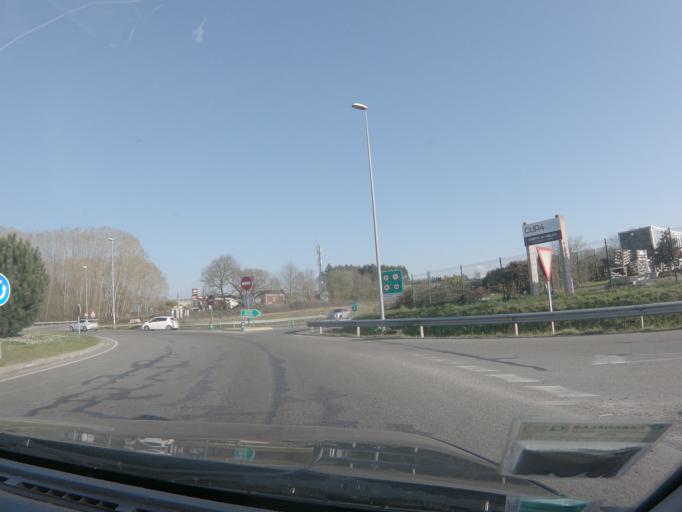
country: ES
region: Galicia
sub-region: Provincia de Lugo
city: Lugo
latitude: 42.9678
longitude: -7.5007
